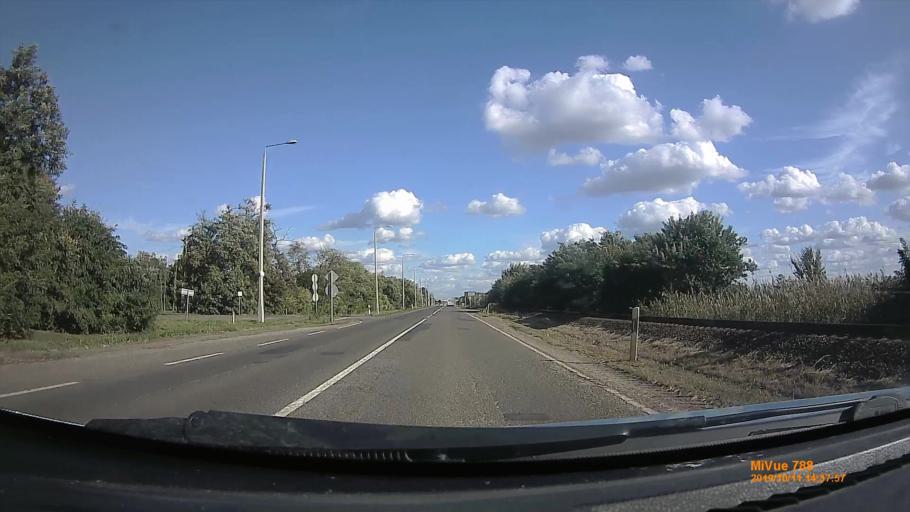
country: HU
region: Hajdu-Bihar
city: Ebes
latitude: 47.5523
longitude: 21.5349
